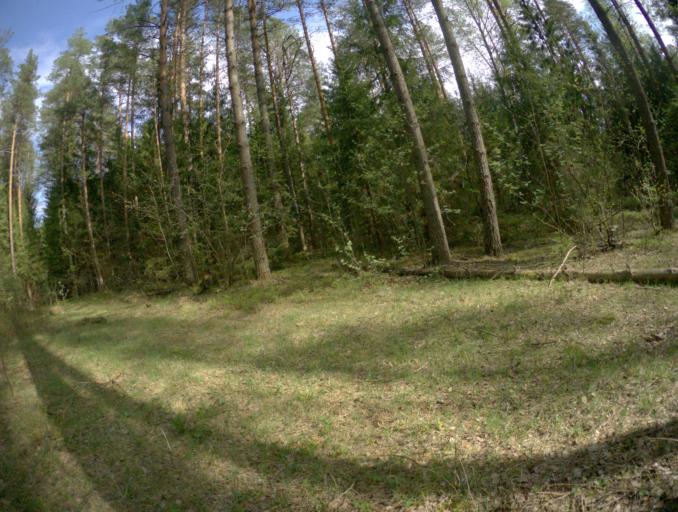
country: RU
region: Vladimir
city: Golovino
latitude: 55.9043
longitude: 40.4877
